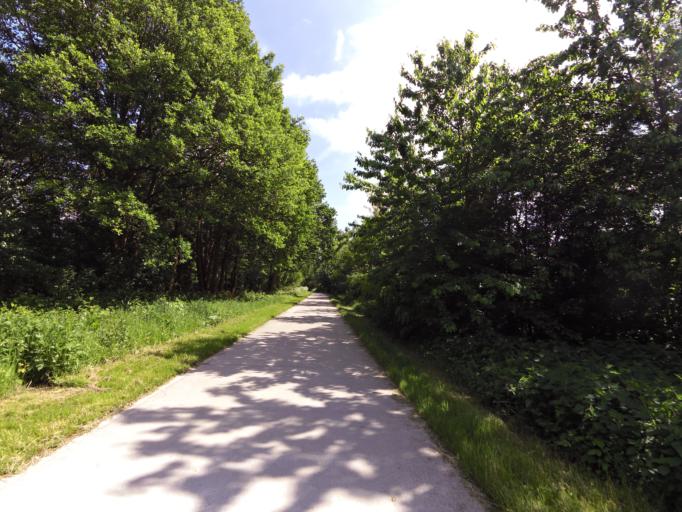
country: BE
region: Flanders
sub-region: Provincie West-Vlaanderen
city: Beernem
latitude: 51.1290
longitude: 3.3439
